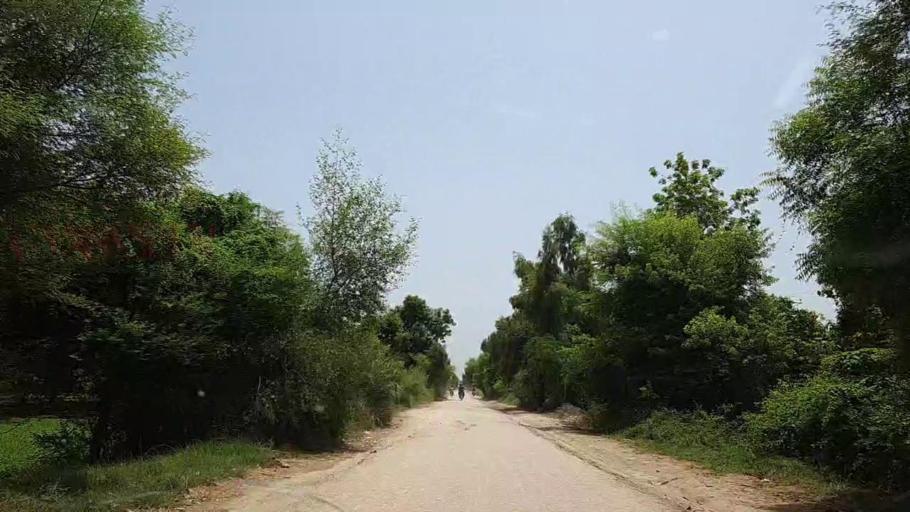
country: PK
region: Sindh
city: Tharu Shah
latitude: 26.9675
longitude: 68.0438
